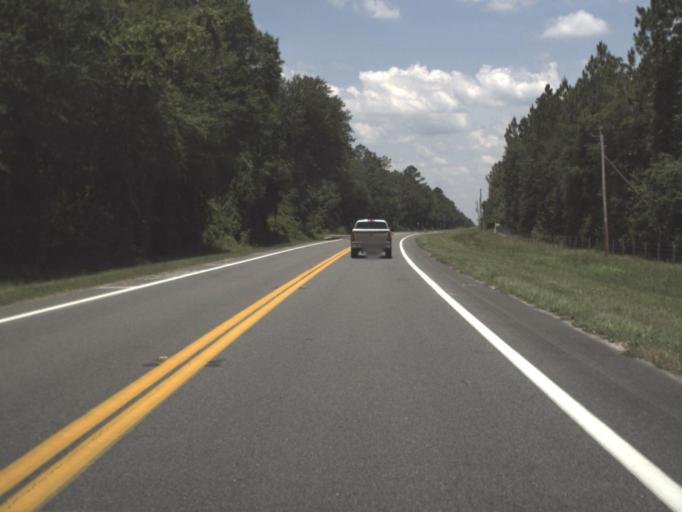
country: US
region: Florida
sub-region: Union County
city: Lake Butler
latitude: 30.0589
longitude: -82.4210
